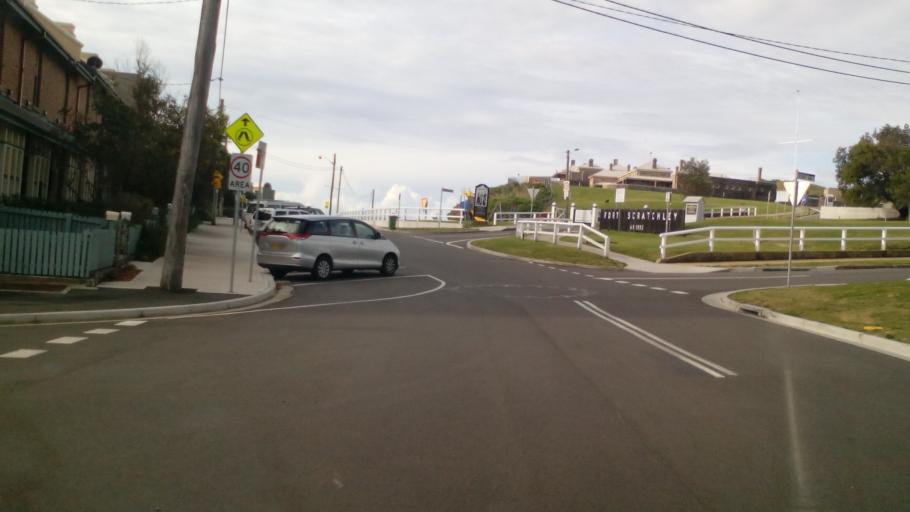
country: AU
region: New South Wales
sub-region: Newcastle
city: Newcastle
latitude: -32.9273
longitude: 151.7896
